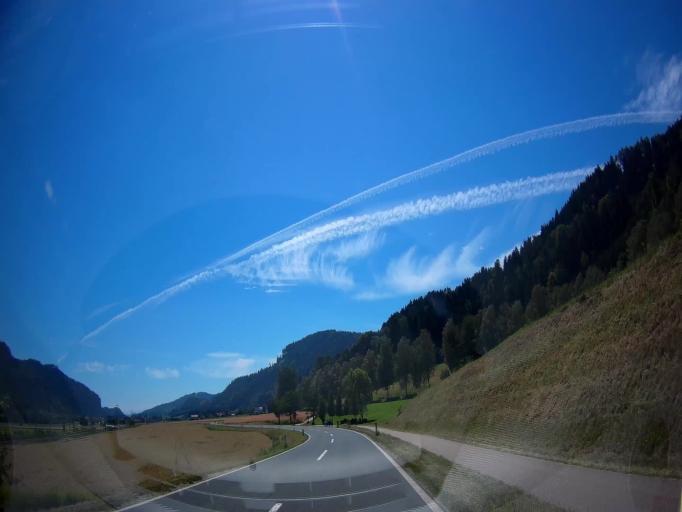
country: AT
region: Carinthia
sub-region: Politischer Bezirk Sankt Veit an der Glan
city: Micheldorf
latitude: 46.9259
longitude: 14.4277
